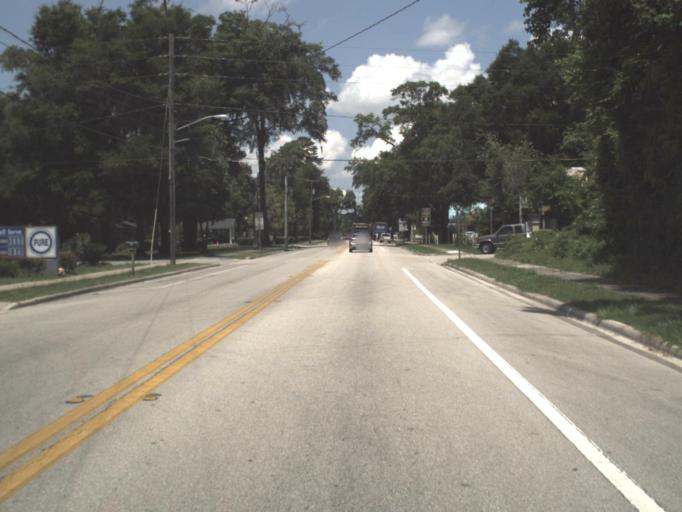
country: US
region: Florida
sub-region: Alachua County
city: High Springs
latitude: 29.8250
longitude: -82.5922
